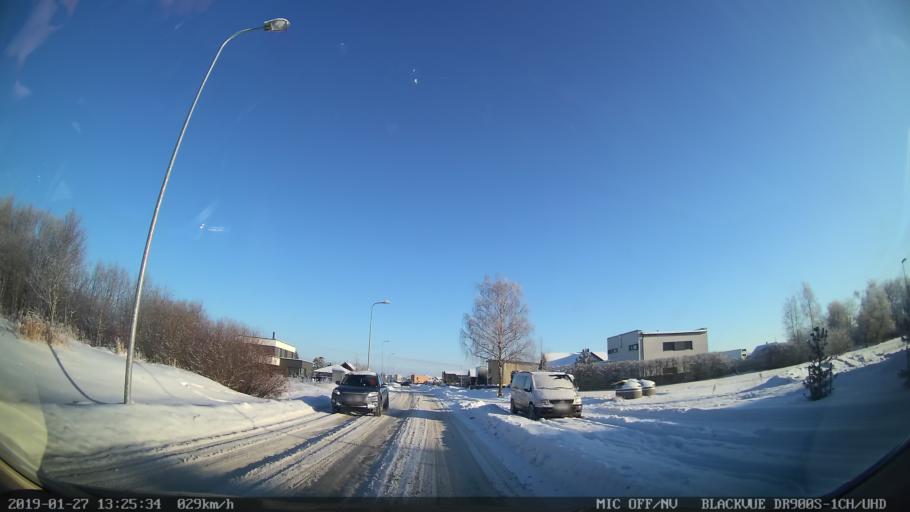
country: EE
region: Harju
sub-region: Tallinna linn
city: Tallinn
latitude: 59.3961
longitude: 24.7973
